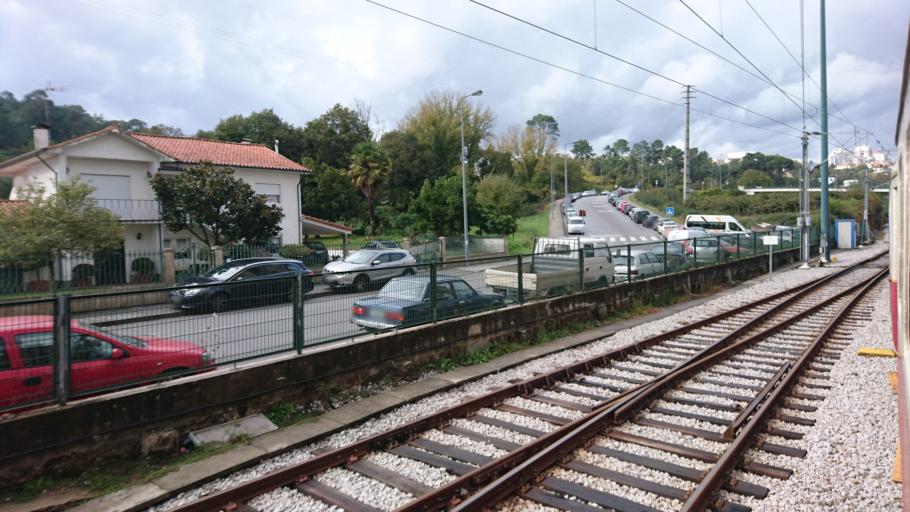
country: PT
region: Porto
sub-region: Marco de Canaveses
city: Marco de Canavezes
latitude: 41.1820
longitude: -8.1377
